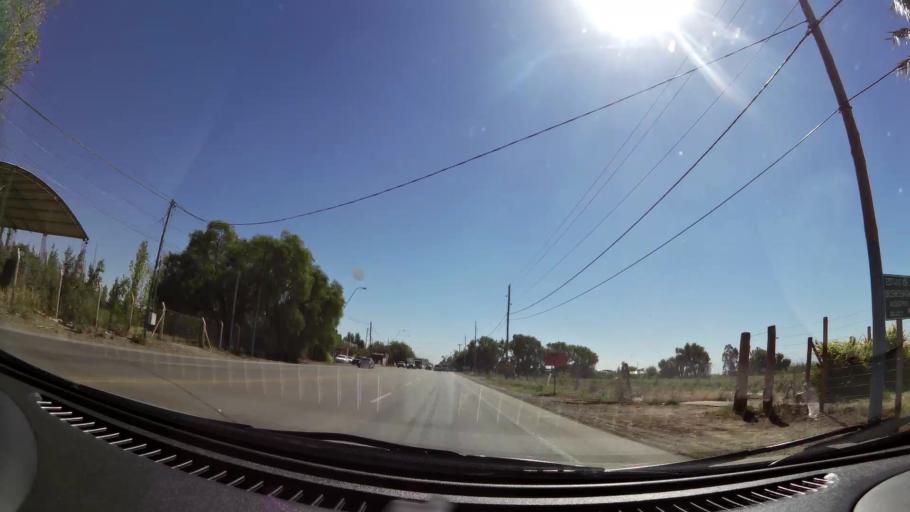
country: AR
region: San Juan
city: Villa Krause
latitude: -31.6143
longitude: -68.5476
